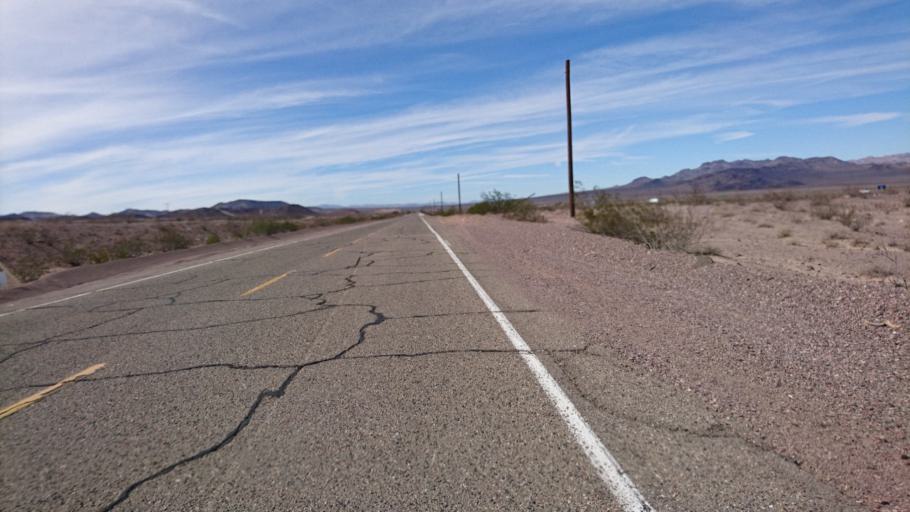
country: US
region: California
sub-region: San Bernardino County
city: Twentynine Palms
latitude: 34.7243
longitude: -116.1453
